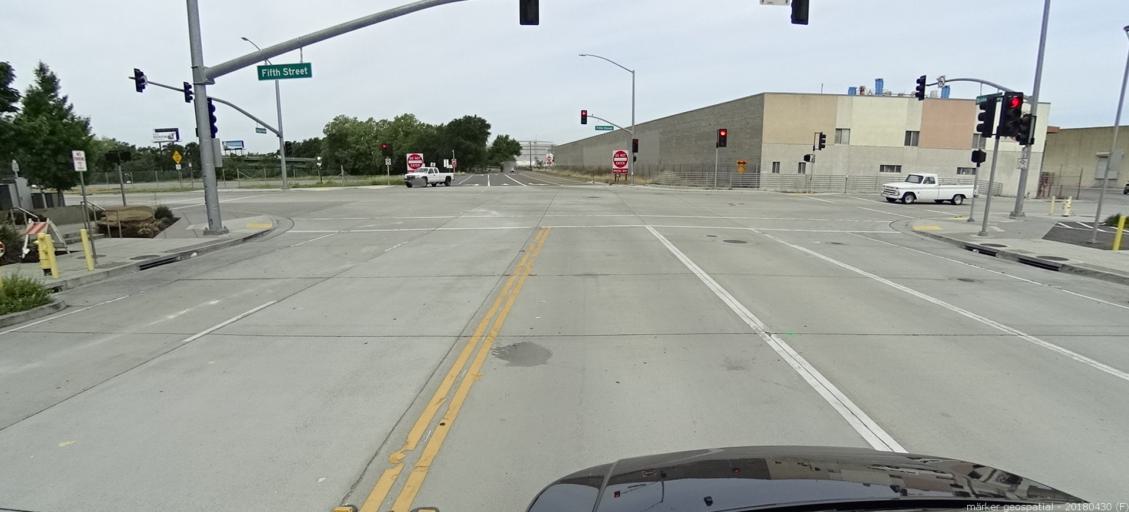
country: US
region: California
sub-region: Yolo County
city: West Sacramento
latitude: 38.5767
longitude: -121.5165
